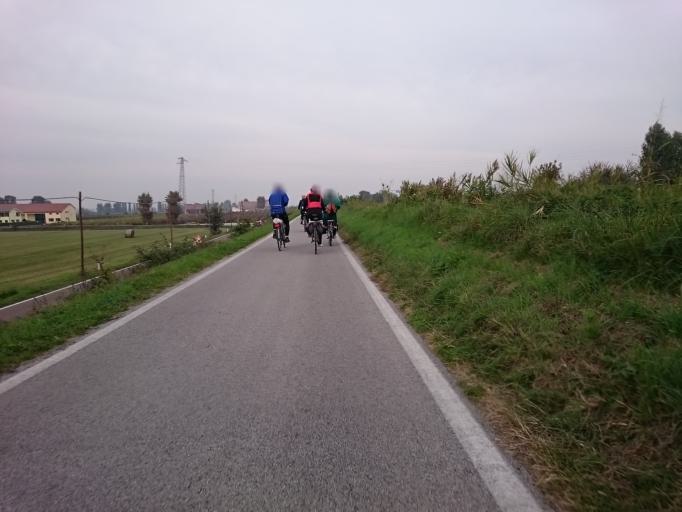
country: IT
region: Veneto
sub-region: Provincia di Padova
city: Battaglia Terme
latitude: 45.2987
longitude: 11.7914
